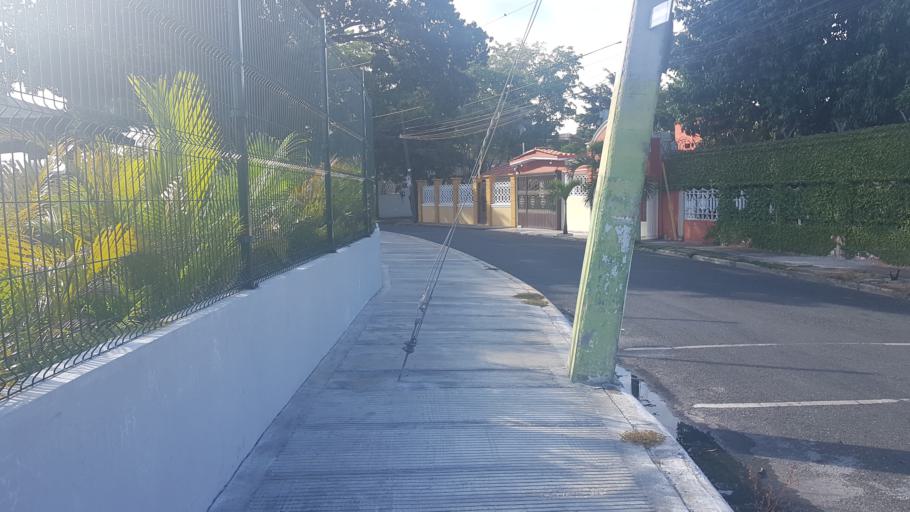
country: DO
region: Santo Domingo
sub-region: Santo Domingo
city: Santo Domingo Este
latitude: 18.4872
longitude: -69.8464
